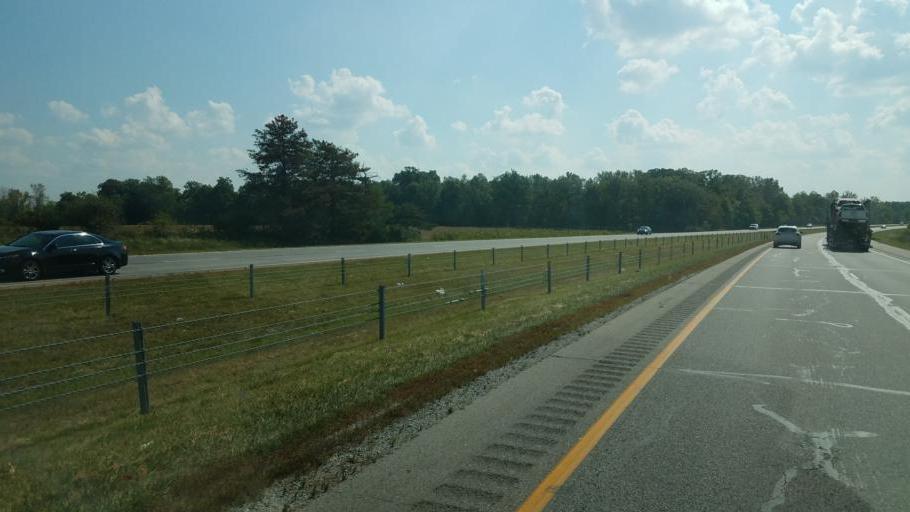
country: US
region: Indiana
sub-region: Allen County
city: Leo-Cedarville
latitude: 41.2609
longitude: -85.0868
